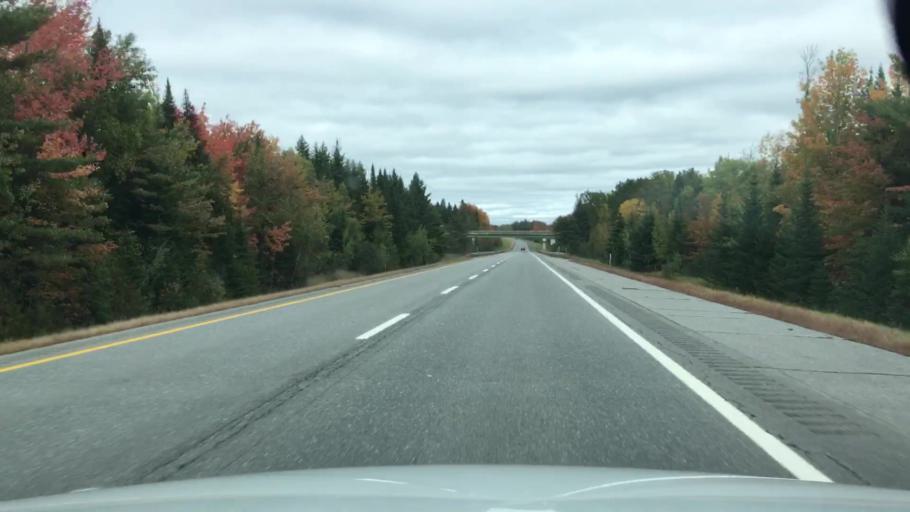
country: US
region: Maine
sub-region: Waldo County
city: Burnham
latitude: 44.7028
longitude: -69.4578
